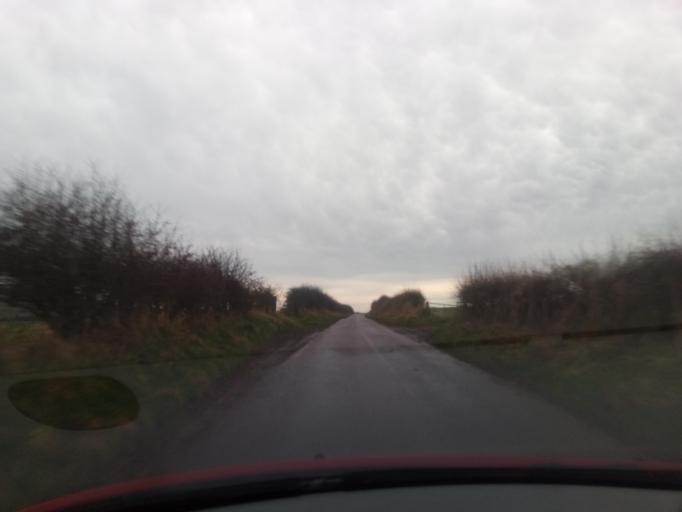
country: GB
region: England
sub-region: Northumberland
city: Wooler
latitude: 55.4993
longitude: -1.9195
